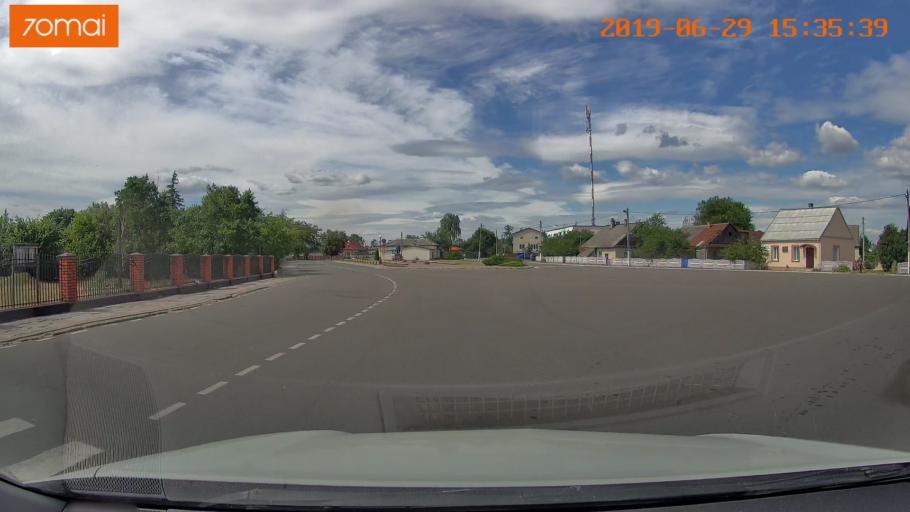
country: BY
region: Brest
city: Mikashevichy
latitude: 52.2160
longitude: 27.4715
